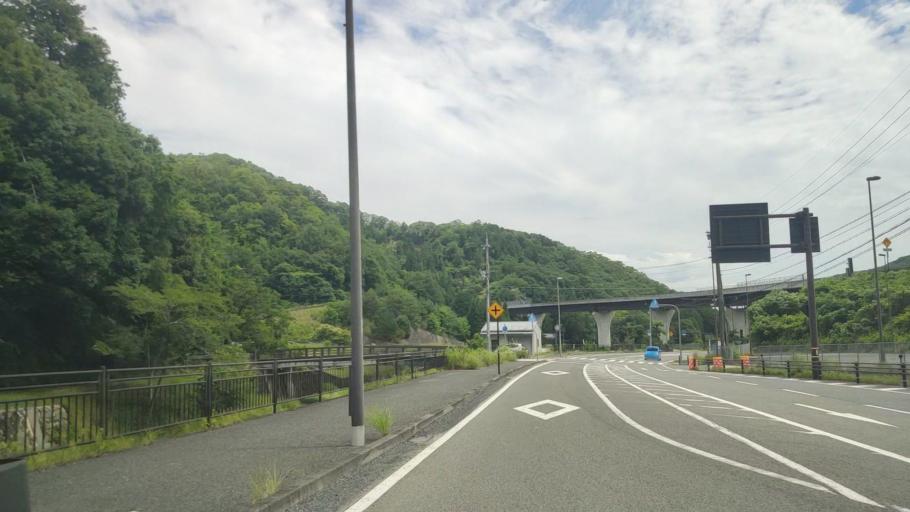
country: JP
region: Hyogo
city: Yamazakicho-nakabirose
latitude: 35.0583
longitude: 134.3663
